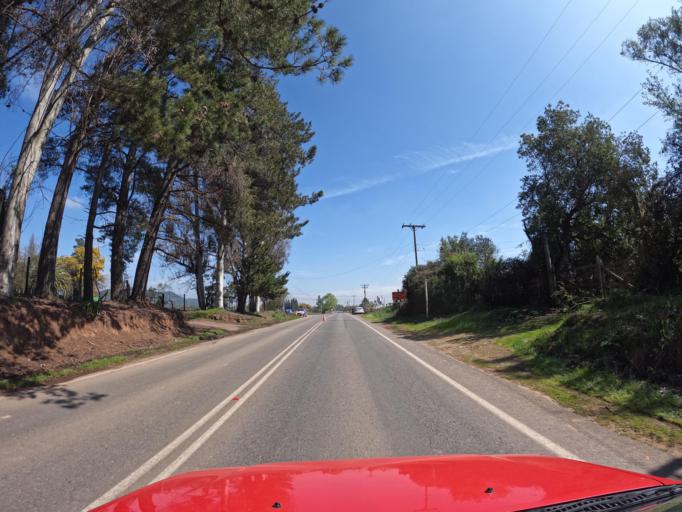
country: CL
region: Maule
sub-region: Provincia de Talca
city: San Clemente
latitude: -35.4855
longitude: -71.2792
